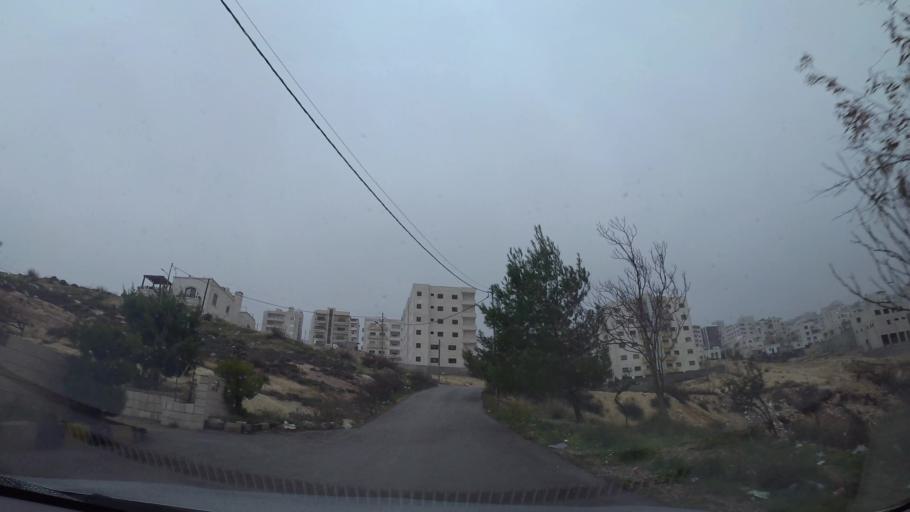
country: JO
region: Amman
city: Al Jubayhah
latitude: 32.0374
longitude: 35.8511
